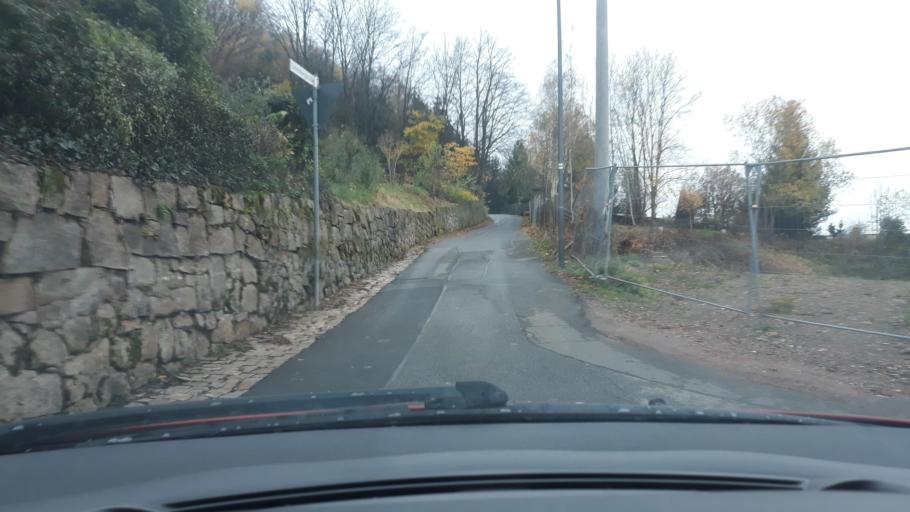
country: DE
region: Saxony
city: Kirchberg
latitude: 50.6196
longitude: 12.5260
